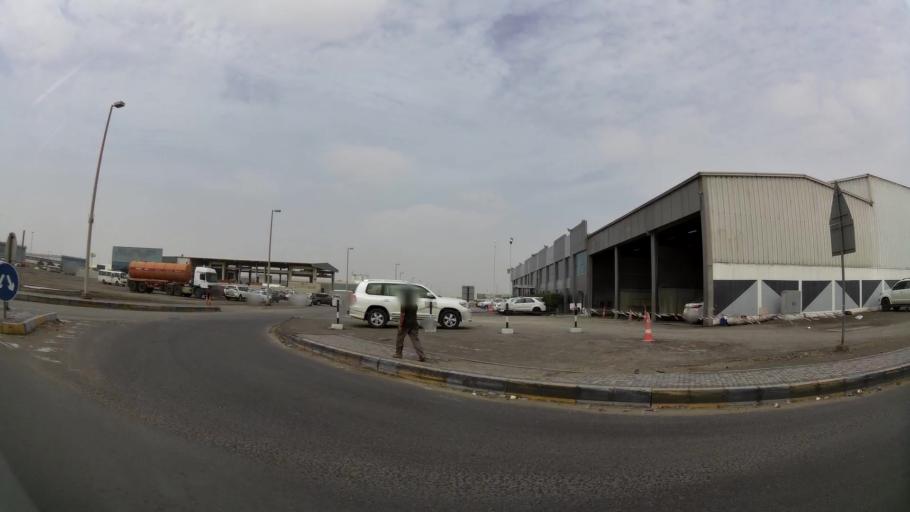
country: AE
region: Abu Dhabi
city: Abu Dhabi
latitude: 24.3539
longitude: 54.4839
